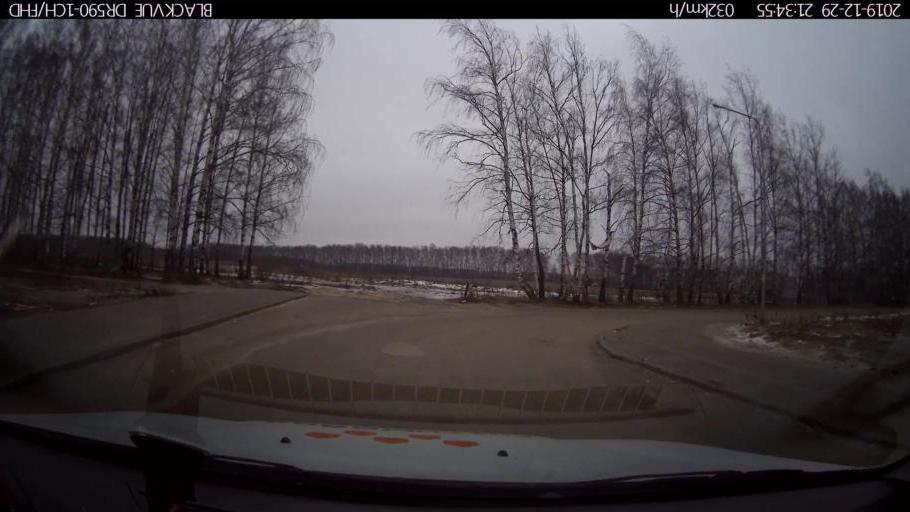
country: RU
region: Nizjnij Novgorod
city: Afonino
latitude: 56.2144
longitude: 44.0233
